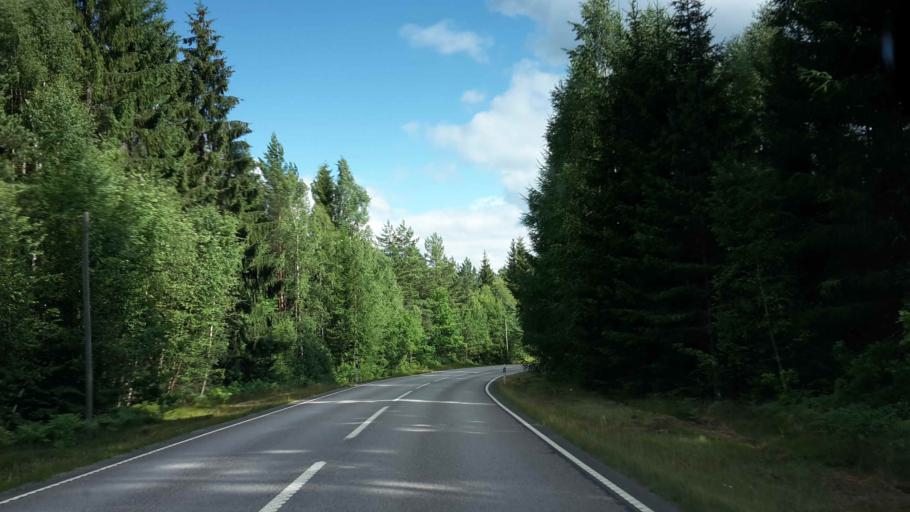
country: SE
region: OErebro
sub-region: Hallsbergs Kommun
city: Palsboda
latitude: 58.8050
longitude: 15.4199
